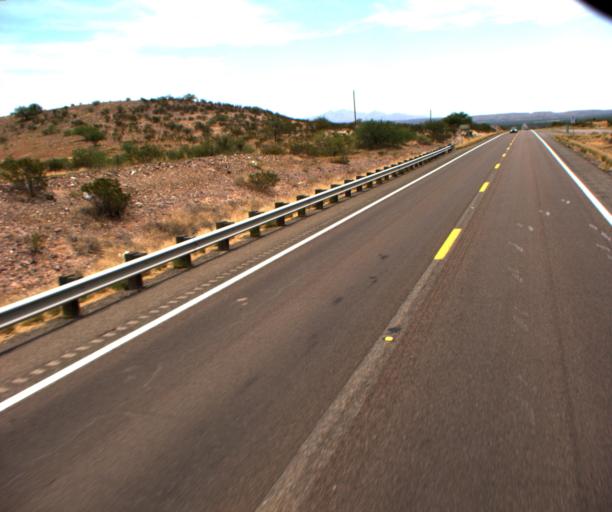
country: US
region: Arizona
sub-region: Graham County
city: Bylas
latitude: 33.1985
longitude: -110.1845
